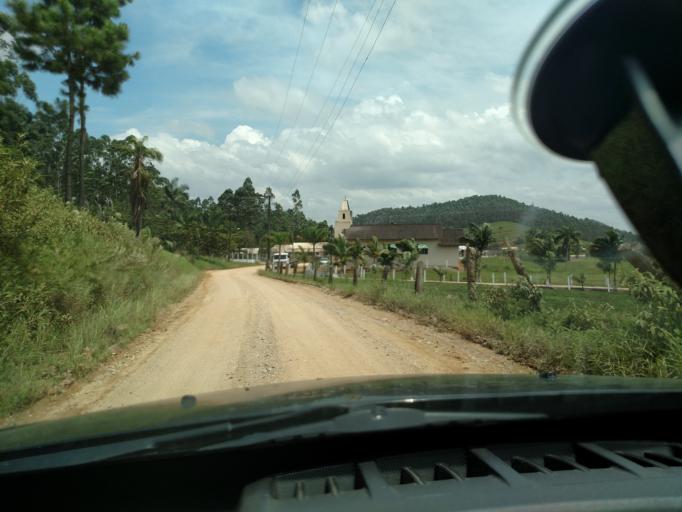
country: BR
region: Santa Catarina
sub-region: Gaspar
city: Gaspar
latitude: -26.9446
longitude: -48.8103
